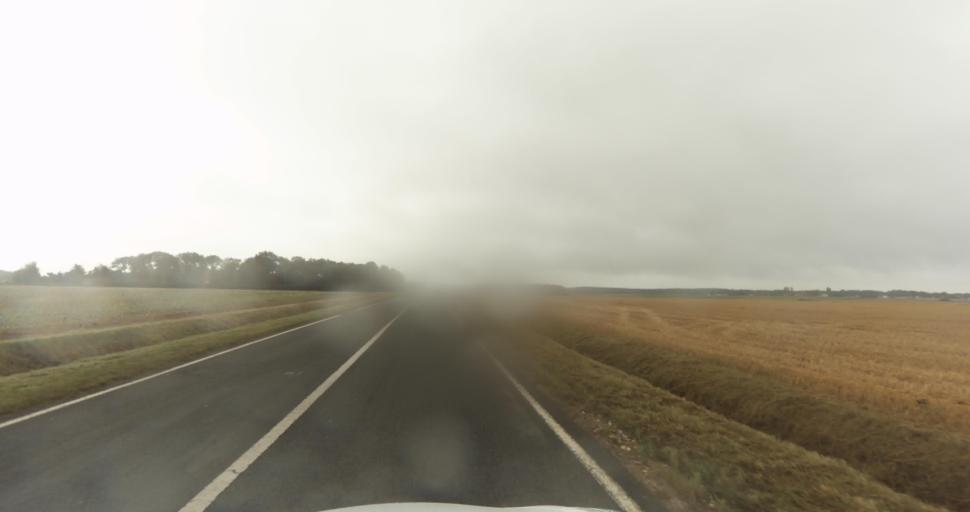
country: FR
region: Haute-Normandie
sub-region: Departement de l'Eure
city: Normanville
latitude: 49.1054
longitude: 1.1713
